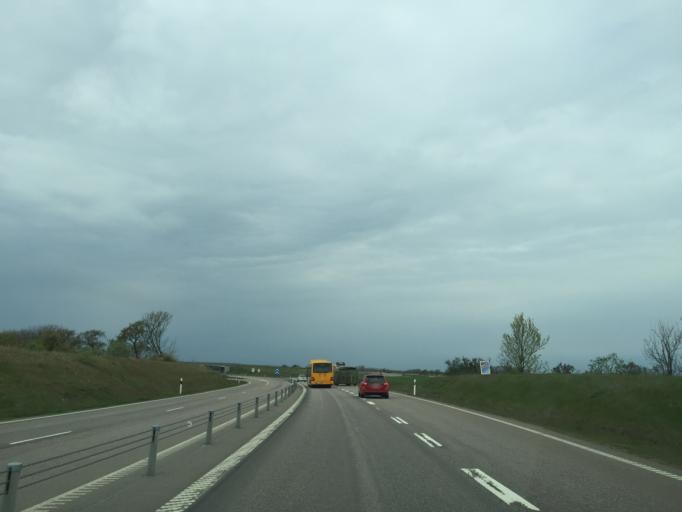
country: SE
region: Skane
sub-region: Hoganas Kommun
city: Hoganas
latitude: 56.1615
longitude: 12.5898
